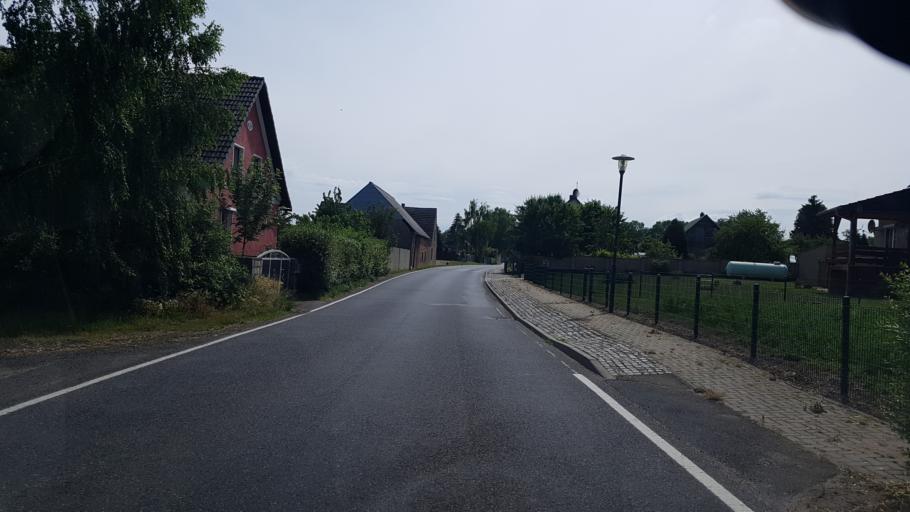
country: DE
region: Brandenburg
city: Prenzlau
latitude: 53.3259
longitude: 13.7906
